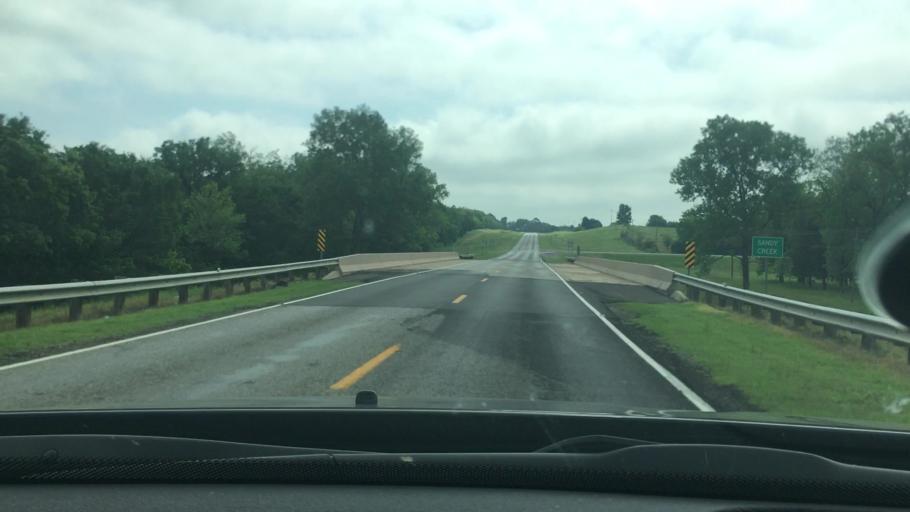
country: US
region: Oklahoma
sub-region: Johnston County
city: Tishomingo
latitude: 34.2304
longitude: -96.6375
